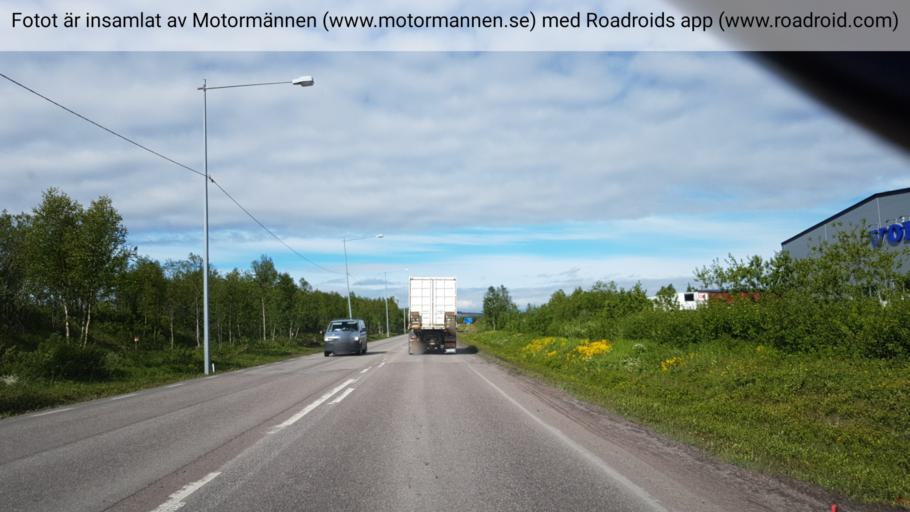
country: SE
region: Norrbotten
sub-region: Kiruna Kommun
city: Kiruna
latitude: 67.8435
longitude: 20.2984
